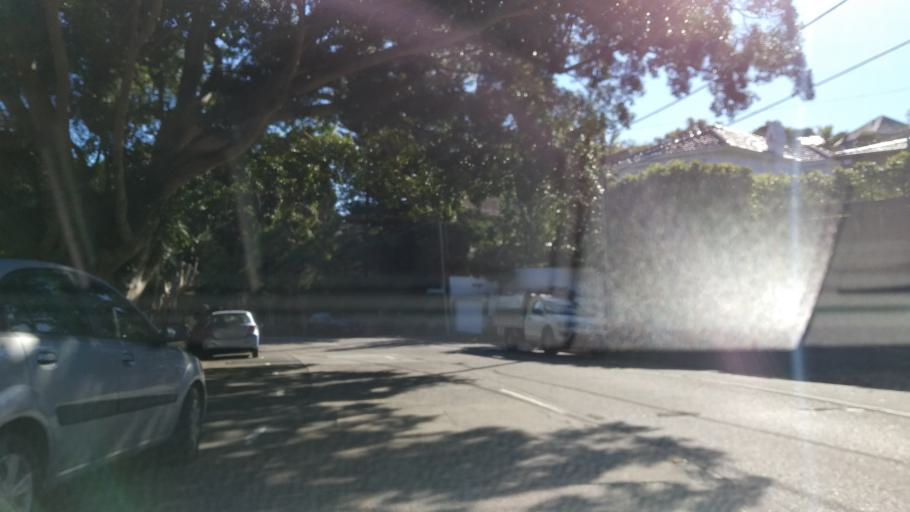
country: AU
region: New South Wales
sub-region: Woollahra
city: Bellevue Hill
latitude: -33.8797
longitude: 151.2484
